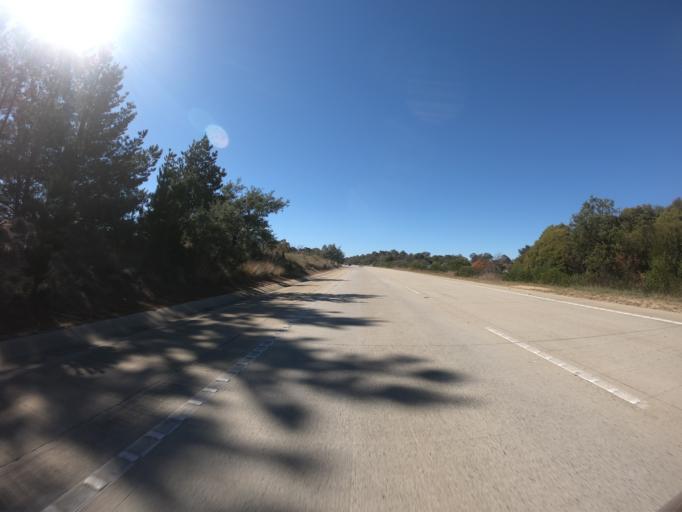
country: AU
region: New South Wales
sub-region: Yass Valley
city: Gundaroo
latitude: -35.1130
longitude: 149.3623
